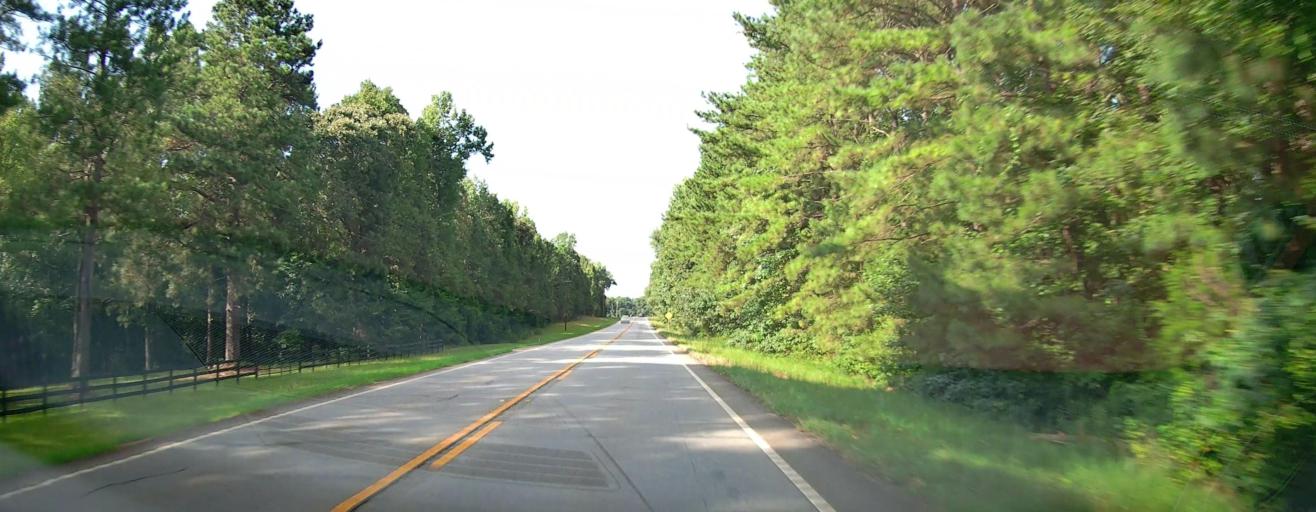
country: US
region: Georgia
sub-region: Coweta County
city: Senoia
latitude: 33.2159
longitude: -84.5789
